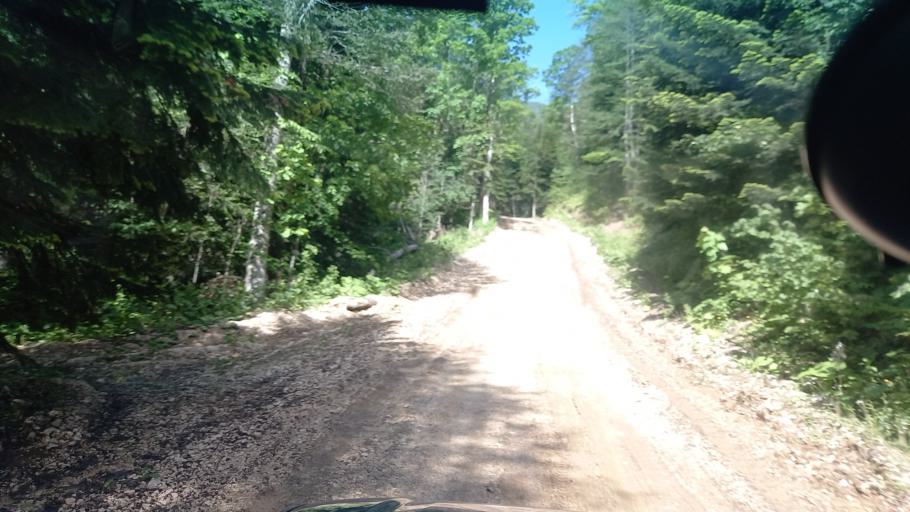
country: RU
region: Krasnodarskiy
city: Neftegorsk
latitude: 44.0150
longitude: 39.8487
